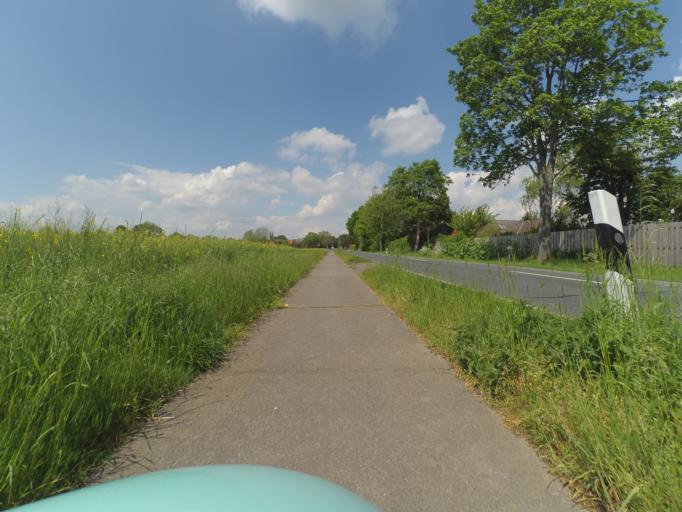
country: DE
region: Lower Saxony
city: Hohenhameln
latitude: 52.2562
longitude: 10.0751
